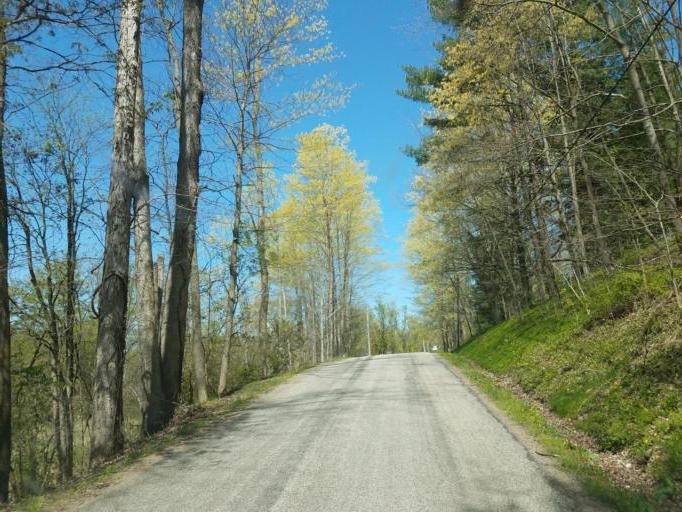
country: US
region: Ohio
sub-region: Richland County
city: Lincoln Heights
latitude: 40.7271
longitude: -82.3999
